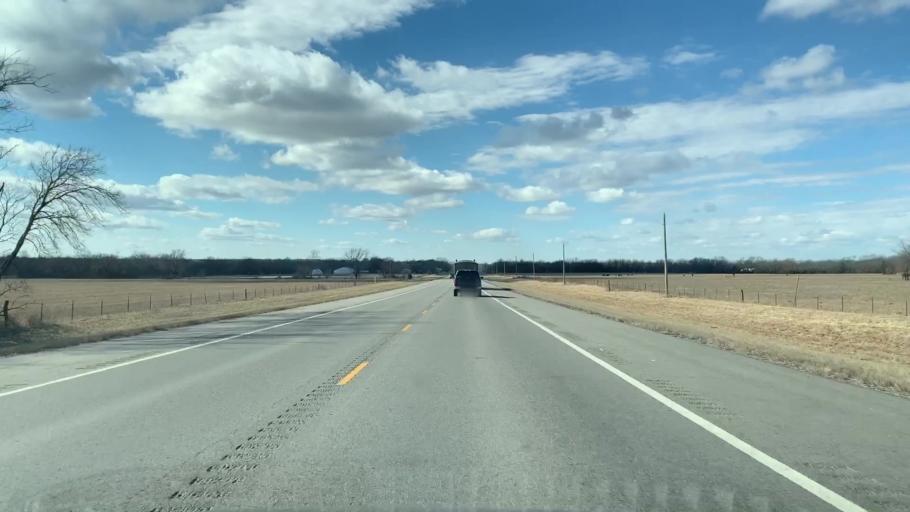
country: US
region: Kansas
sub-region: Cherokee County
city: Columbus
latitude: 37.3400
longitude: -94.9136
